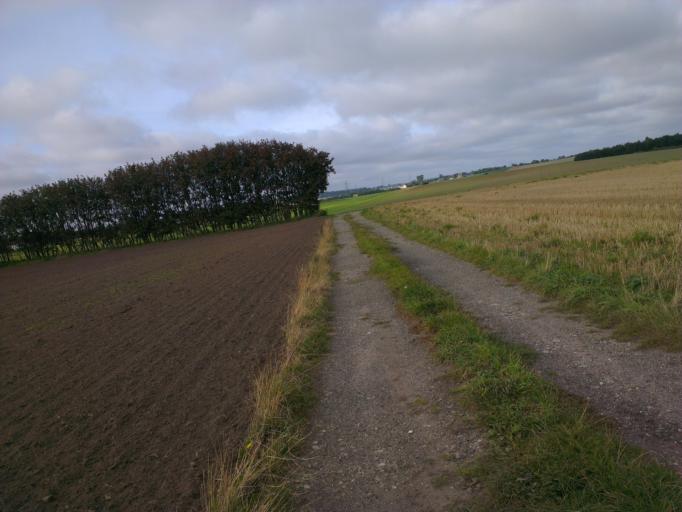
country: DK
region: Capital Region
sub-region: Frederikssund Kommune
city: Jaegerspris
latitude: 55.8081
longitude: 12.0115
